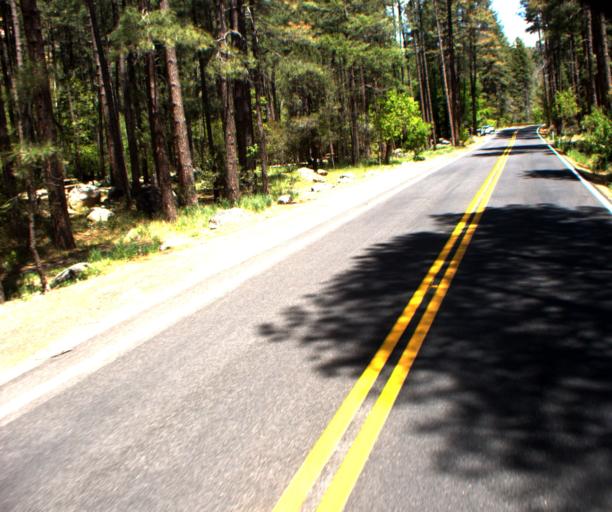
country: US
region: Arizona
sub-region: Coconino County
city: Kachina Village
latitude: 35.0132
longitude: -111.7379
